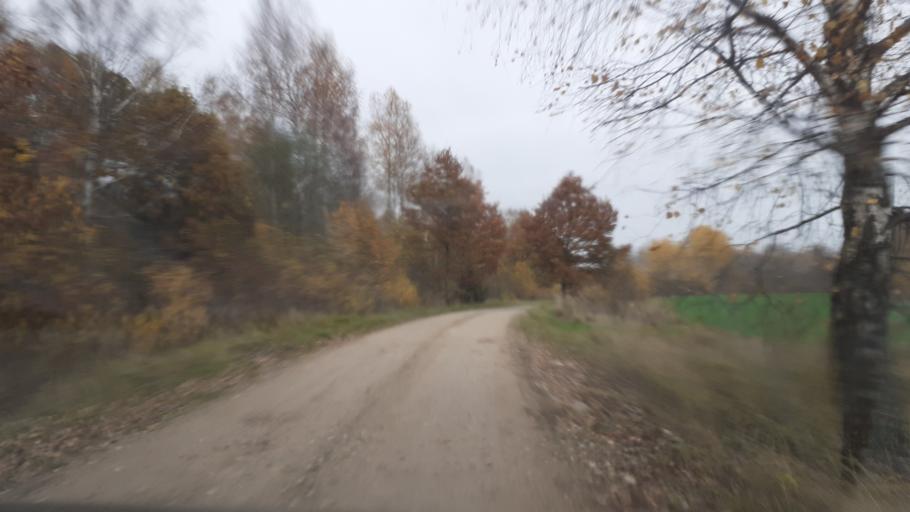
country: LV
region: Saldus Rajons
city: Saldus
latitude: 56.8605
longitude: 22.3435
